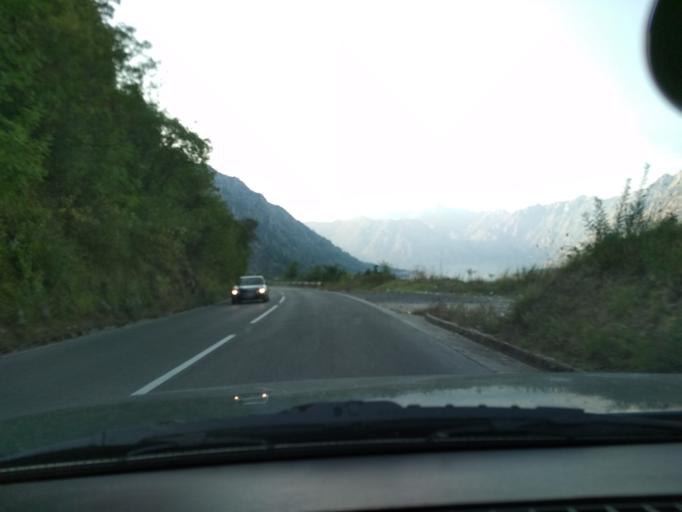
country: ME
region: Kotor
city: Kotor
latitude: 42.4108
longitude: 18.7644
